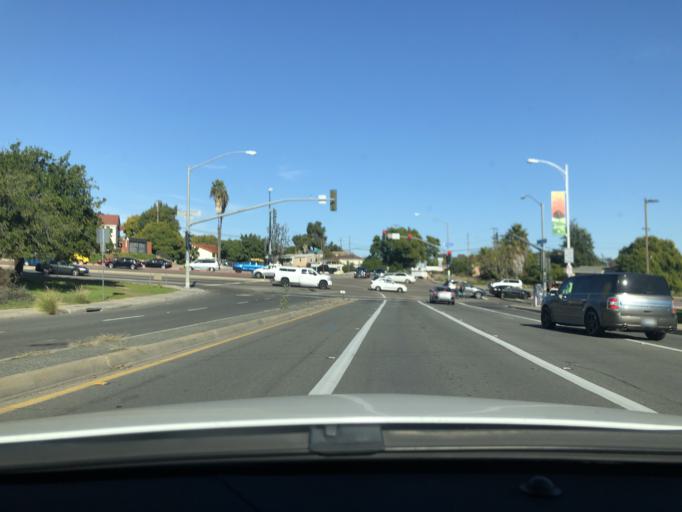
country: US
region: California
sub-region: San Diego County
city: Lemon Grove
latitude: 32.7438
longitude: -117.0542
